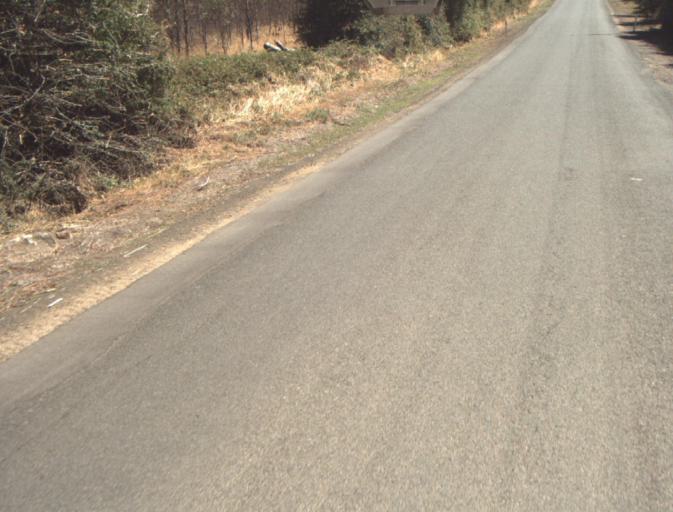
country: AU
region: Tasmania
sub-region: Launceston
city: Newstead
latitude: -41.3820
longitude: 147.2975
